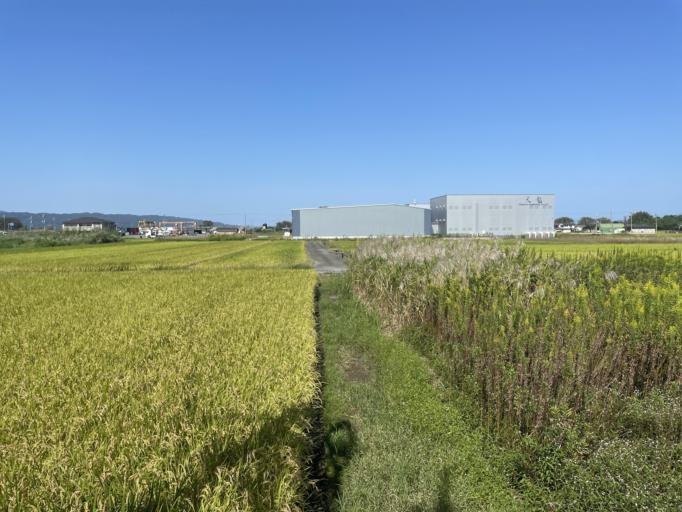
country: JP
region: Nara
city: Tawaramoto
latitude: 34.5697
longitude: 135.7588
